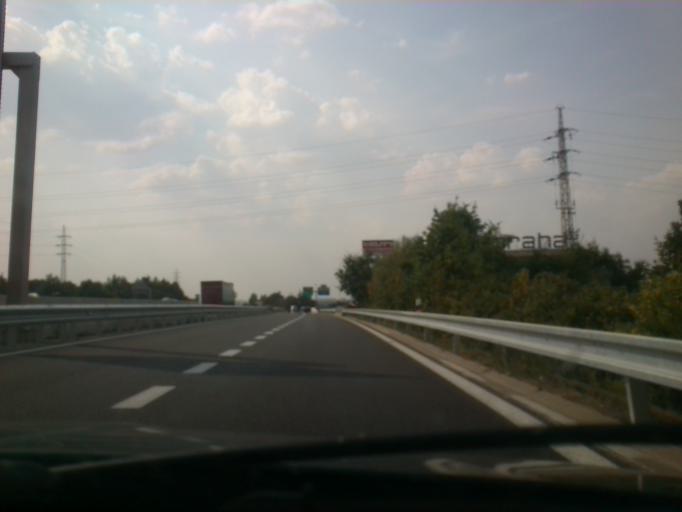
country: CZ
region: Central Bohemia
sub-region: Okres Praha-Zapad
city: Pruhonice
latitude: 50.0050
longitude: 14.5664
